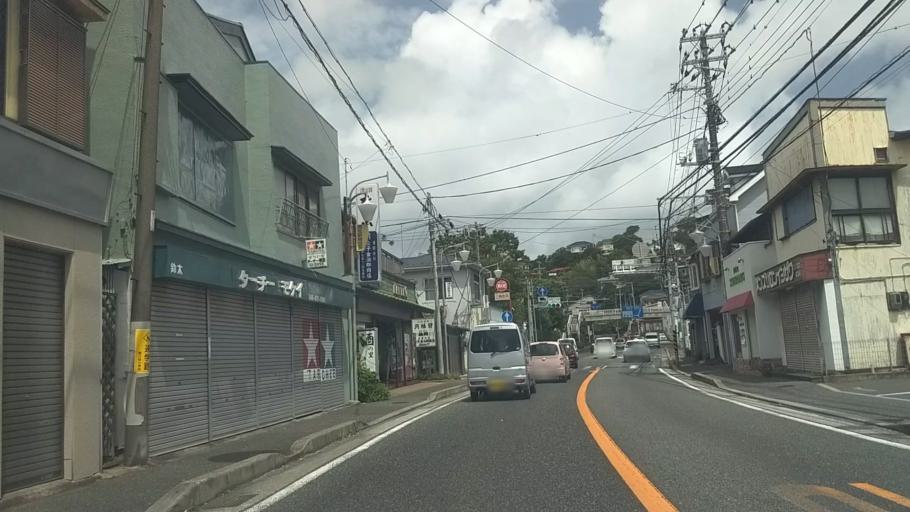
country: JP
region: Kanagawa
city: Yokosuka
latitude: 35.2668
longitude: 139.6682
